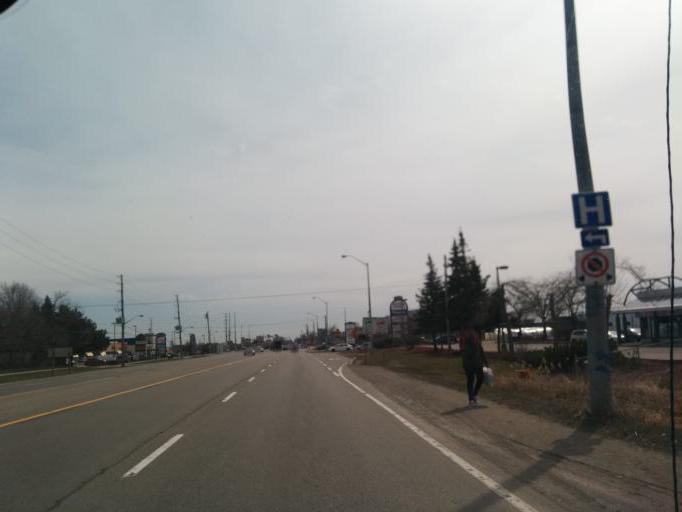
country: CA
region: Ontario
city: Brampton
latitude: 43.7080
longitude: -79.7899
